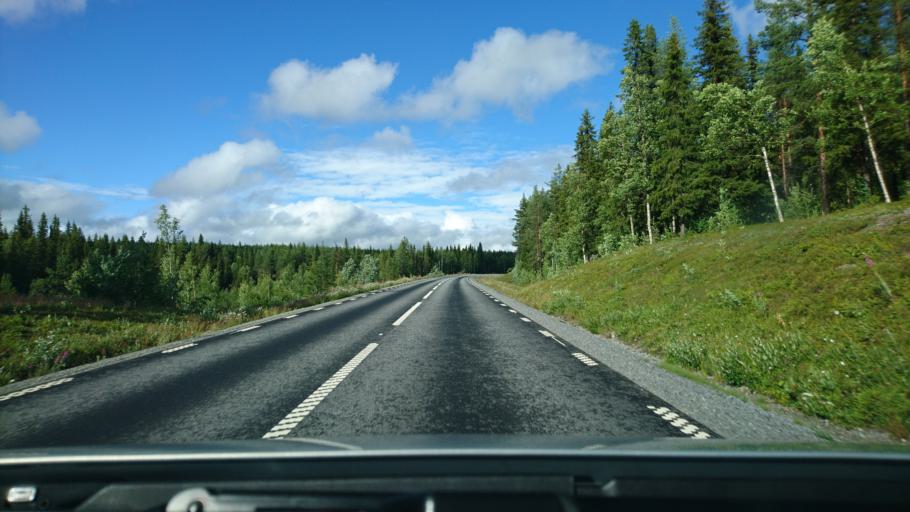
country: SE
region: Vaesterbotten
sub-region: Vilhelmina Kommun
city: Vilhelmina
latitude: 64.6686
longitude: 16.6853
